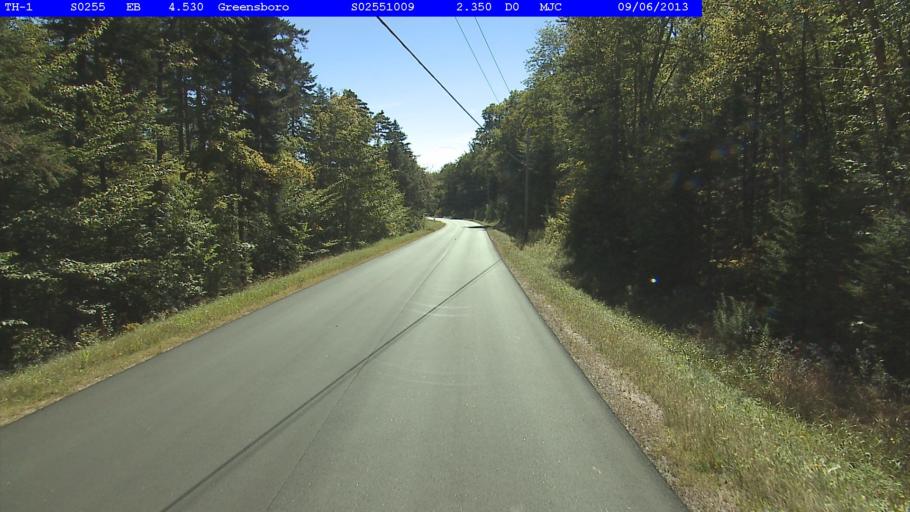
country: US
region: Vermont
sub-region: Caledonia County
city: Hardwick
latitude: 44.6093
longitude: -72.3189
